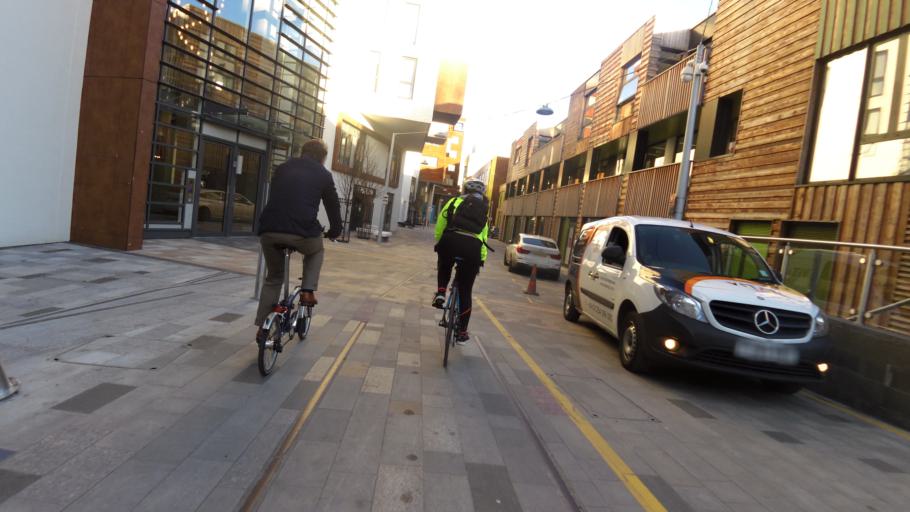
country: GB
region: England
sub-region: Greater London
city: Blackheath
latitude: 51.4773
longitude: -0.0172
